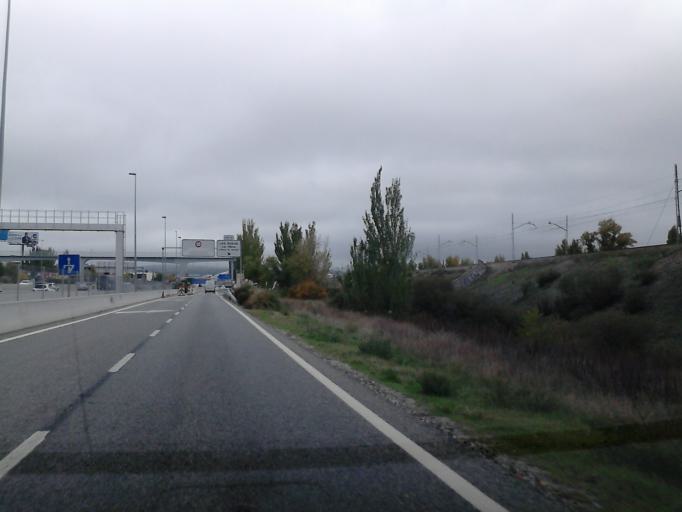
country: ES
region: Madrid
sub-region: Provincia de Madrid
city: Las Matas
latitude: 40.5402
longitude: -3.8914
